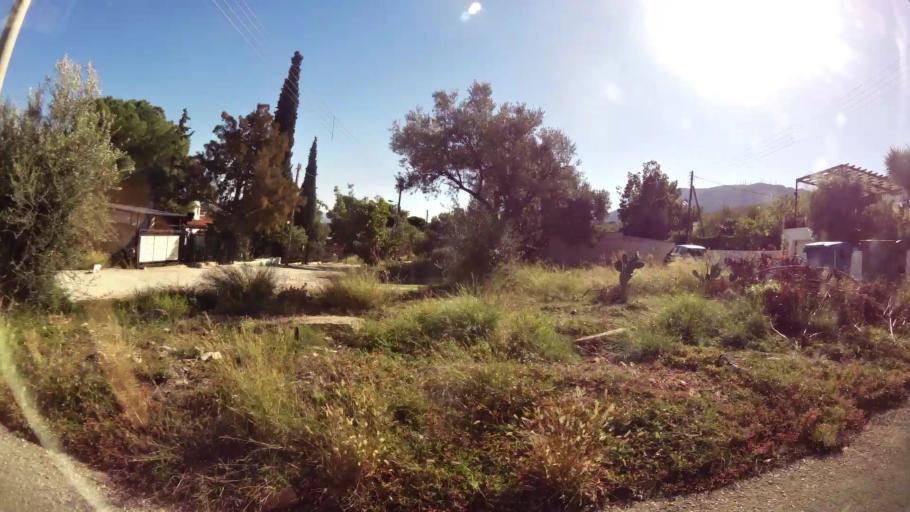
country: GR
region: Attica
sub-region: Nomarchia Anatolikis Attikis
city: Leondarion
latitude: 37.9858
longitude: 23.8429
